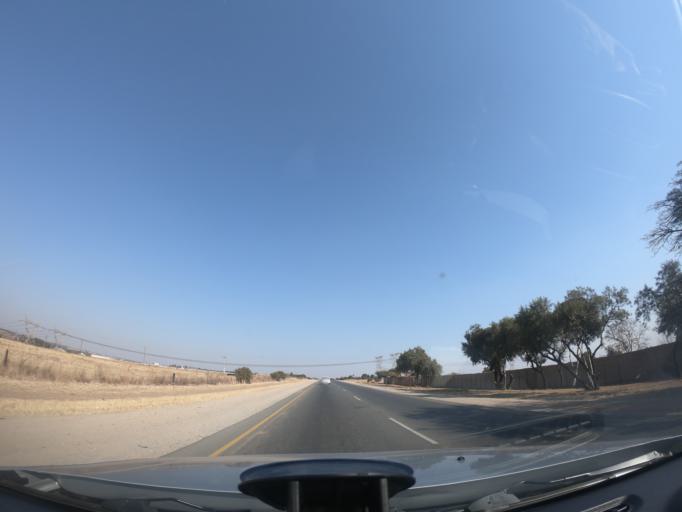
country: ZA
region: Gauteng
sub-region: City of Johannesburg Metropolitan Municipality
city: Diepsloot
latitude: -25.8947
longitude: 28.0273
